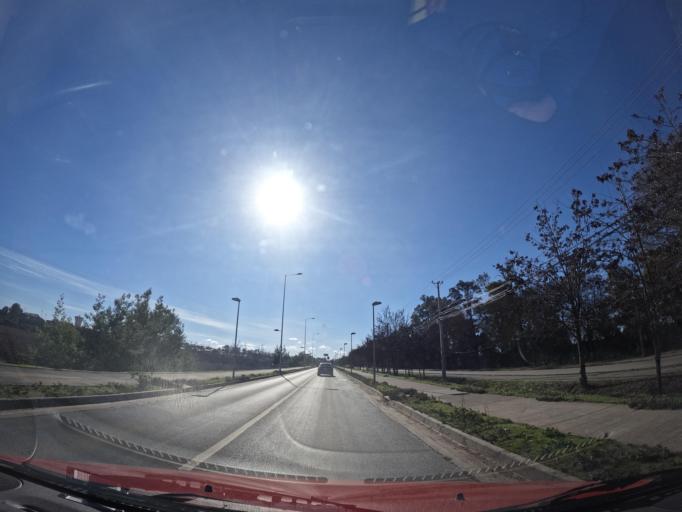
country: CL
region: Maule
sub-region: Provincia de Cauquenes
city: Cauquenes
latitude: -35.9773
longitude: -72.3155
